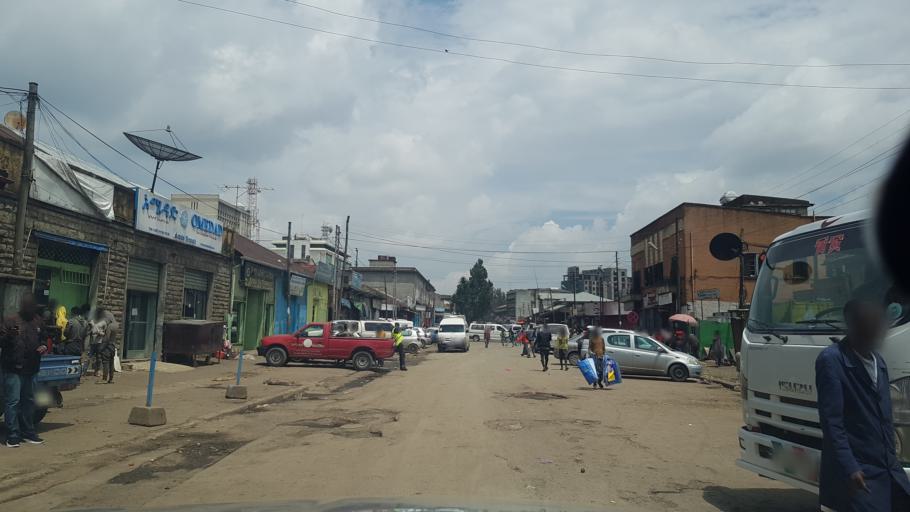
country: ET
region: Adis Abeba
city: Addis Ababa
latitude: 9.0340
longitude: 38.7486
